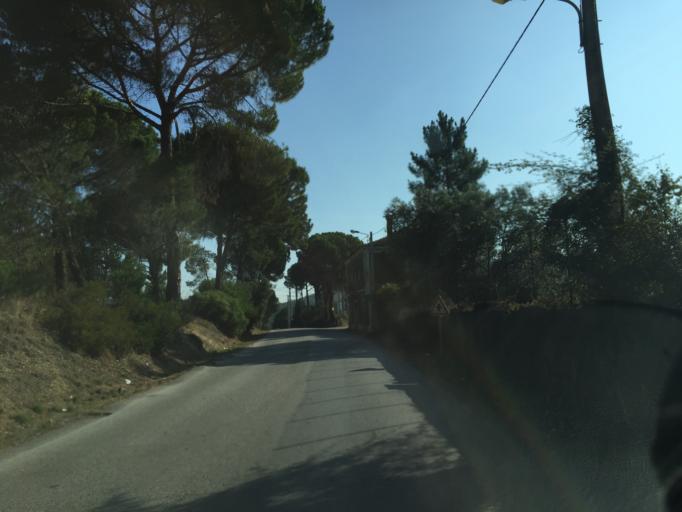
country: PT
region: Santarem
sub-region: Abrantes
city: Alferrarede
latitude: 39.4860
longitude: -8.1806
